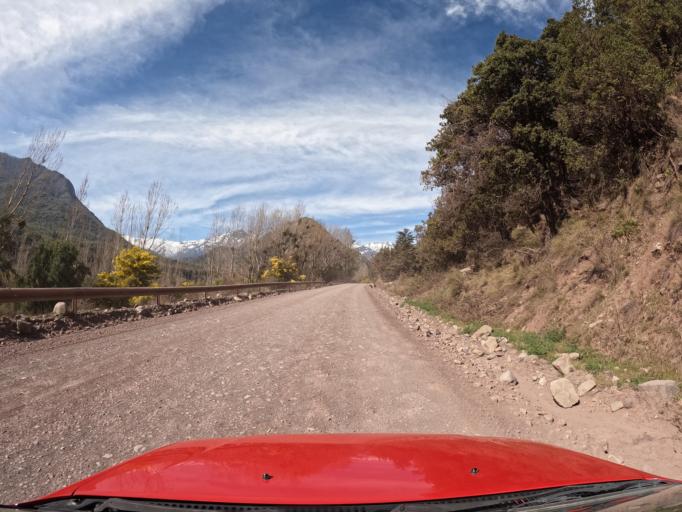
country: CL
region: O'Higgins
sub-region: Provincia de Colchagua
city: Chimbarongo
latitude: -35.0008
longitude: -70.7769
